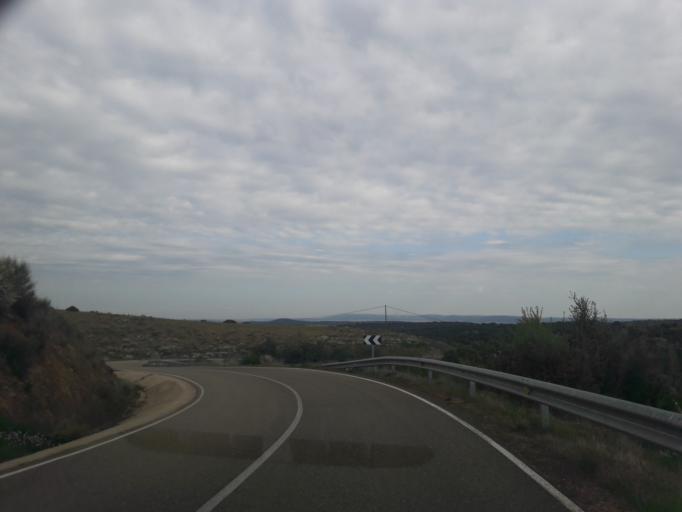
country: ES
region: Castille and Leon
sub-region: Provincia de Salamanca
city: Pastores
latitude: 40.5180
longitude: -6.5147
